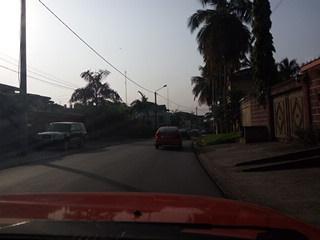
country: CI
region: Lagunes
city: Abobo
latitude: 5.3760
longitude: -3.9891
